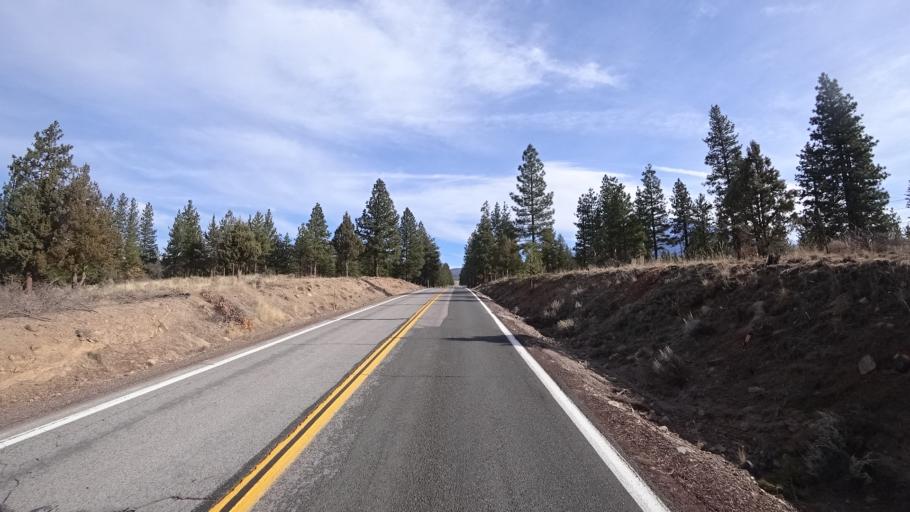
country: US
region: California
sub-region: Siskiyou County
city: Weed
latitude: 41.4940
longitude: -122.3790
